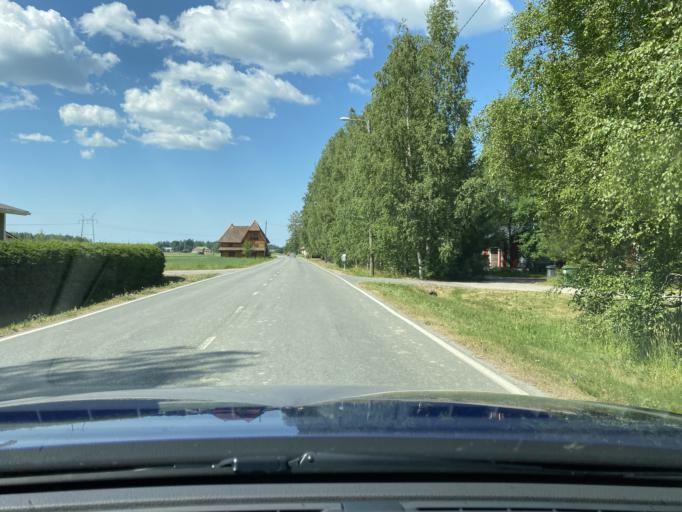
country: FI
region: Satakunta
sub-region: Rauma
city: Eura
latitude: 61.1439
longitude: 22.1147
